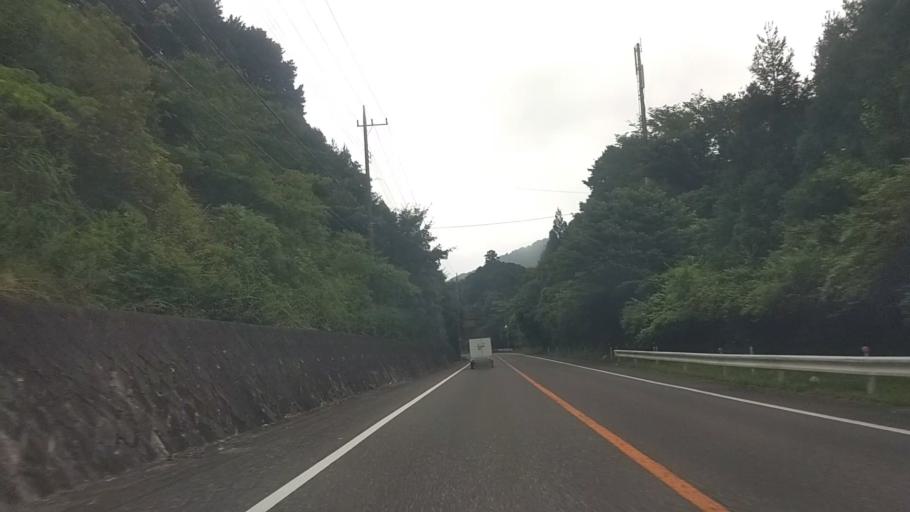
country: JP
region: Chiba
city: Kawaguchi
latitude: 35.1524
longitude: 140.0675
